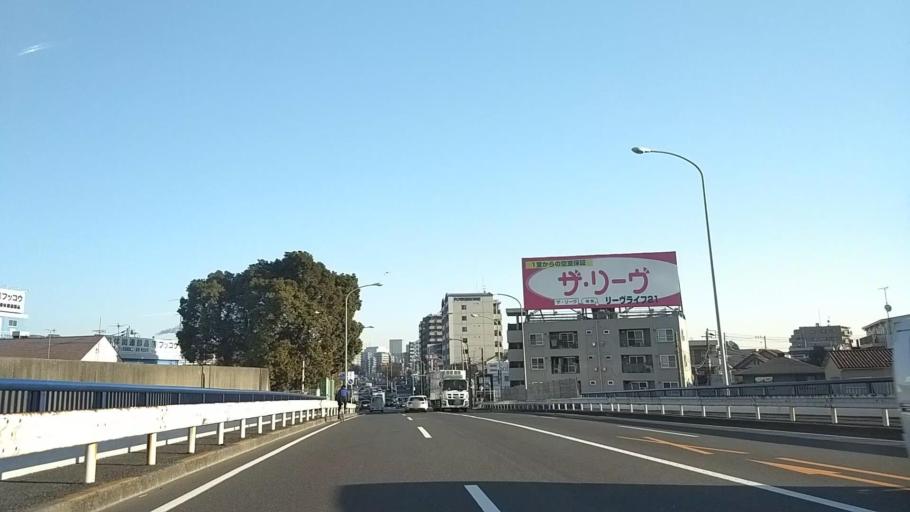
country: JP
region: Kanagawa
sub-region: Kawasaki-shi
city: Kawasaki
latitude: 35.5130
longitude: 139.6854
